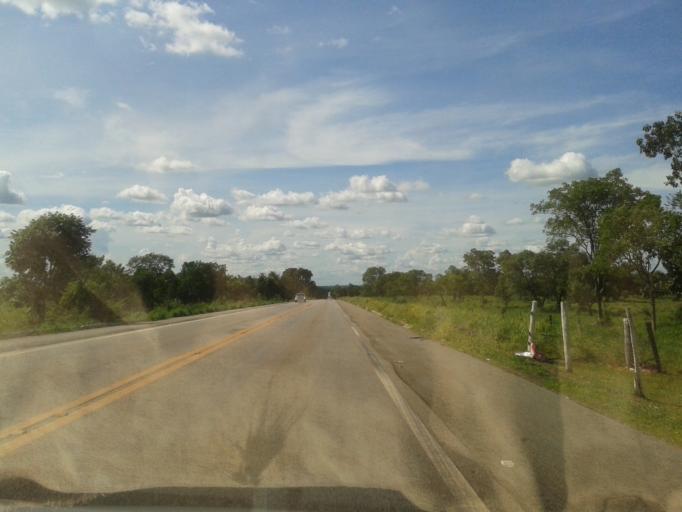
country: BR
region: Goias
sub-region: Mozarlandia
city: Mozarlandia
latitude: -15.2454
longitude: -50.5075
